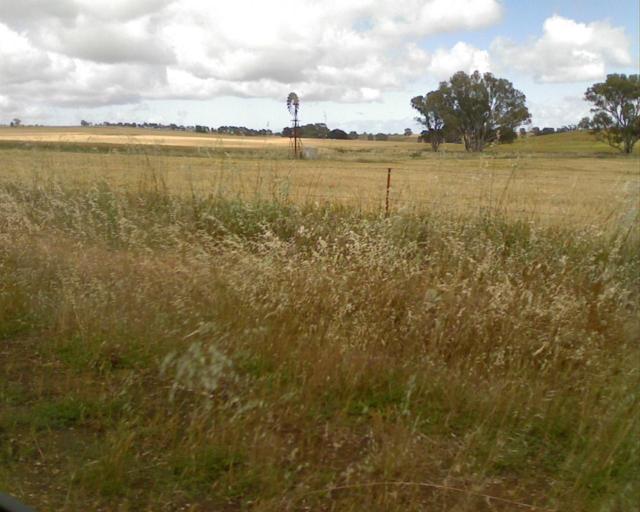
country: AU
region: South Australia
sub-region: Port Pirie City and Dists
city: Solomontown
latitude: -32.9360
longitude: 138.2373
